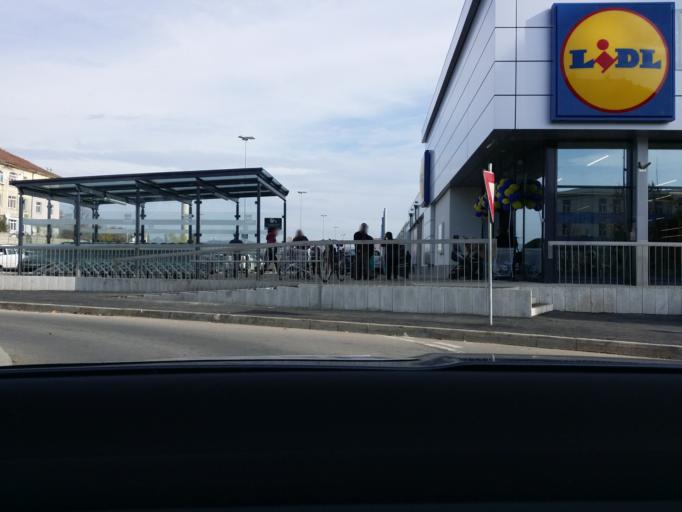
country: RO
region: Prahova
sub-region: Municipiul Campina
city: Campina
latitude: 45.1153
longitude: 25.7445
